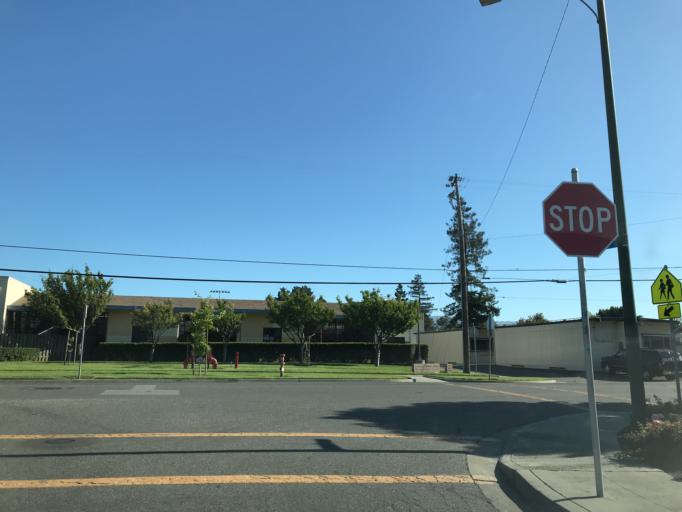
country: US
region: California
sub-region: Santa Clara County
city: Mountain View
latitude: 37.4124
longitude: -122.0862
